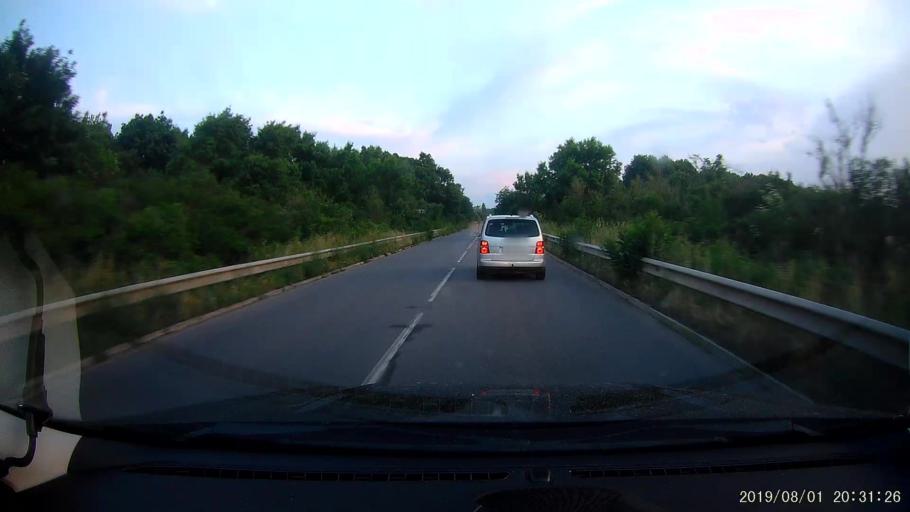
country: BG
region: Yambol
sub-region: Obshtina Elkhovo
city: Elkhovo
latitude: 42.1286
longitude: 26.5397
